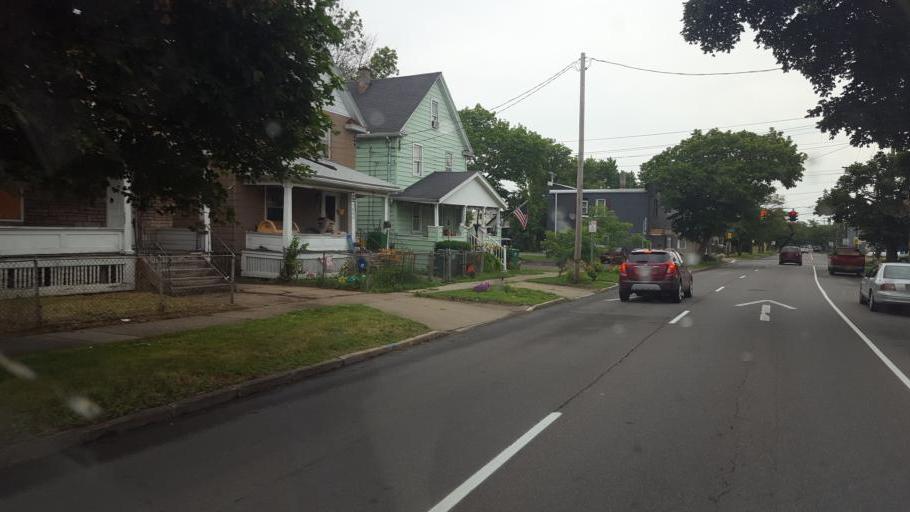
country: US
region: New York
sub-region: Niagara County
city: Niagara Falls
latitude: 43.0914
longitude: -79.0400
